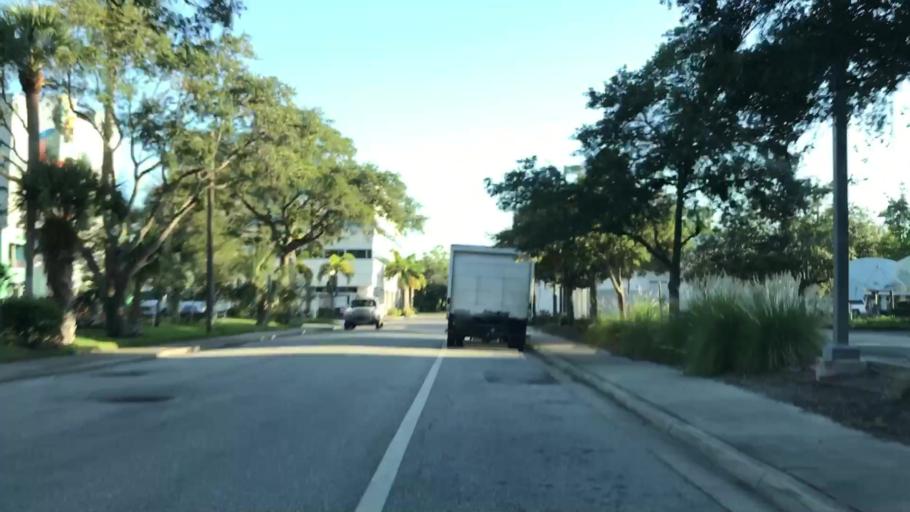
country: US
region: Florida
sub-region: Sarasota County
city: Sarasota
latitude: 27.3373
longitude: -82.5361
